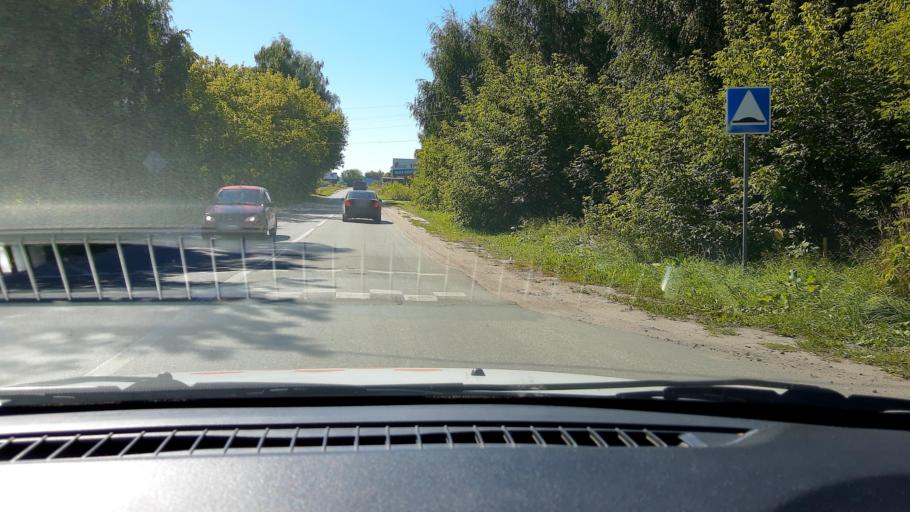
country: RU
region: Nizjnij Novgorod
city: Zavolzh'ye
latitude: 56.7154
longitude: 43.4148
